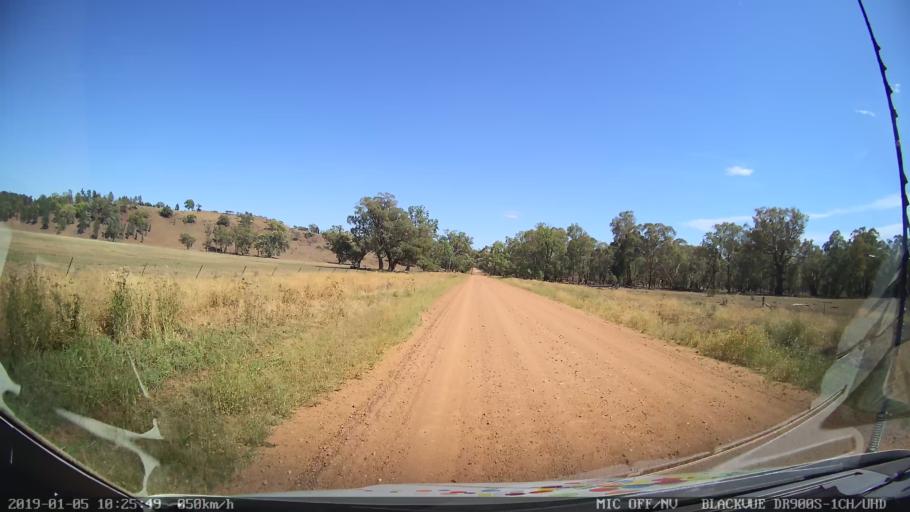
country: AU
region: New South Wales
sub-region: Gilgandra
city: Gilgandra
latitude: -31.5582
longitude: 148.9576
